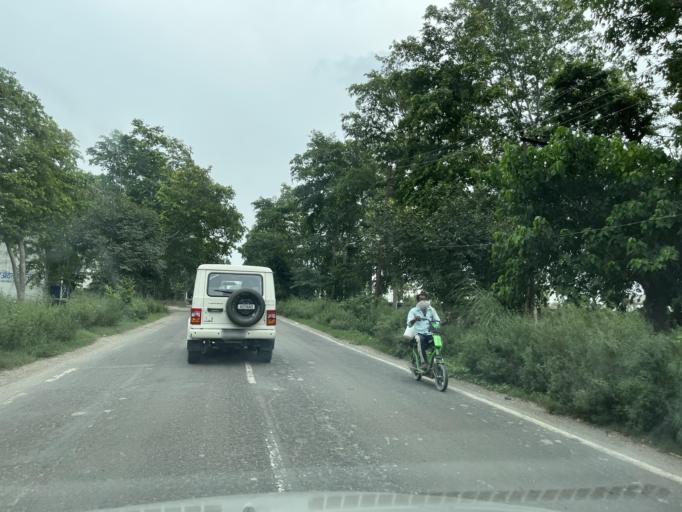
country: IN
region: Uttar Pradesh
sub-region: Rampur
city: Bilaspur
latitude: 29.0279
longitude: 79.2669
